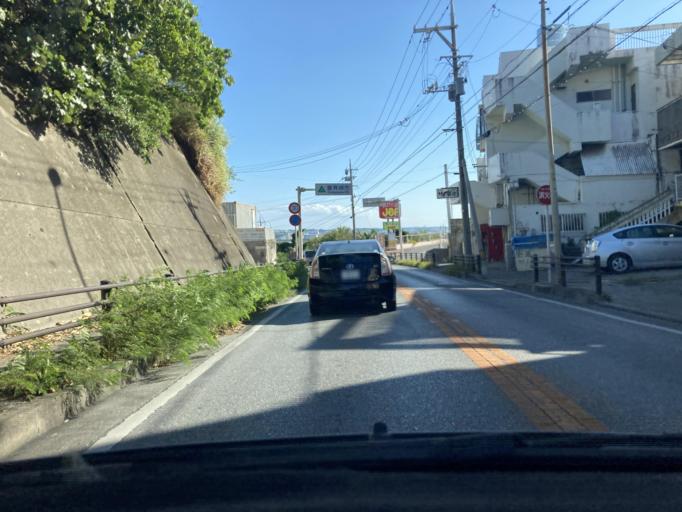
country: JP
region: Okinawa
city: Tomigusuku
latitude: 26.1821
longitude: 127.6622
